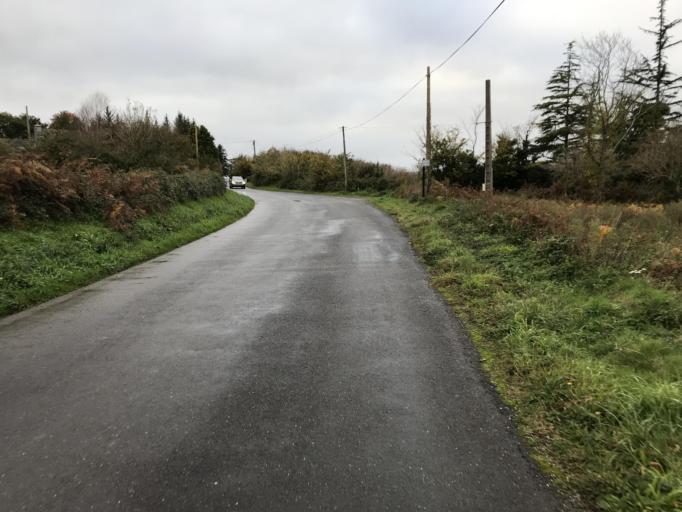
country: FR
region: Brittany
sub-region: Departement du Finistere
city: Logonna-Daoulas
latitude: 48.3344
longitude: -4.3102
